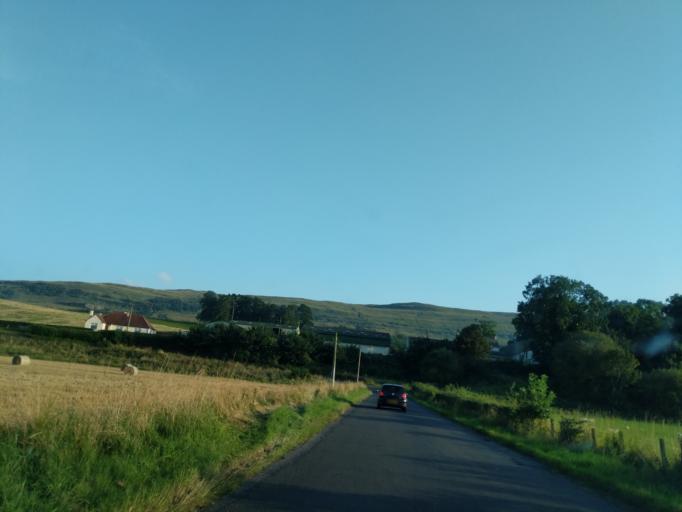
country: GB
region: Scotland
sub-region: Stirling
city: Doune
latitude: 56.1284
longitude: -4.0964
